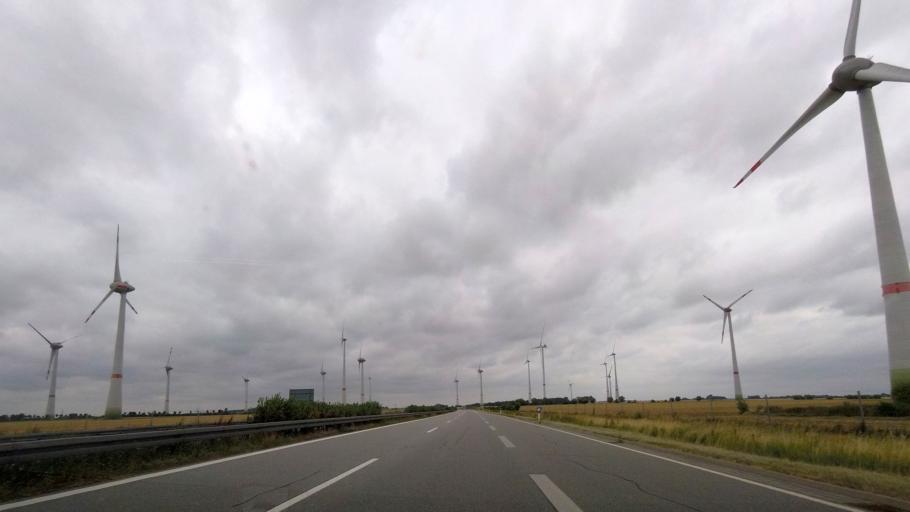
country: DE
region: Mecklenburg-Vorpommern
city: Kessin
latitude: 53.7118
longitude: 13.3305
